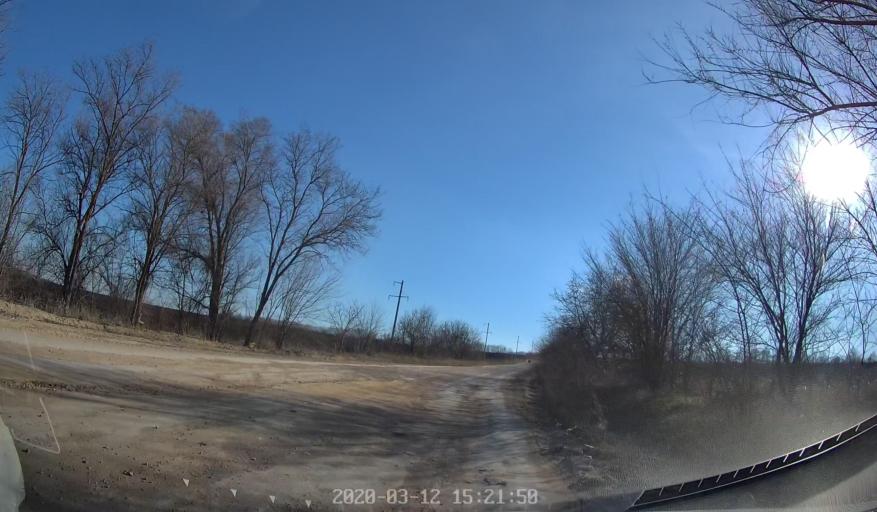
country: MD
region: Chisinau
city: Ciorescu
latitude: 47.2003
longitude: 28.9212
